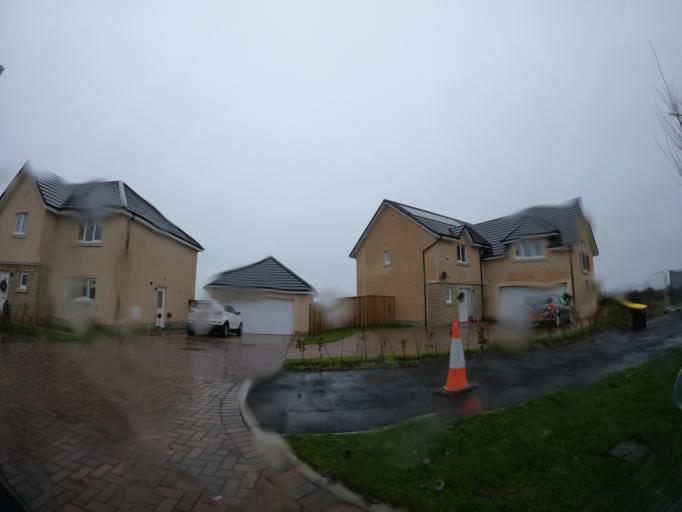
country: GB
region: Scotland
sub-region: West Lothian
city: East Calder
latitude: 55.8911
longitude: -3.4513
